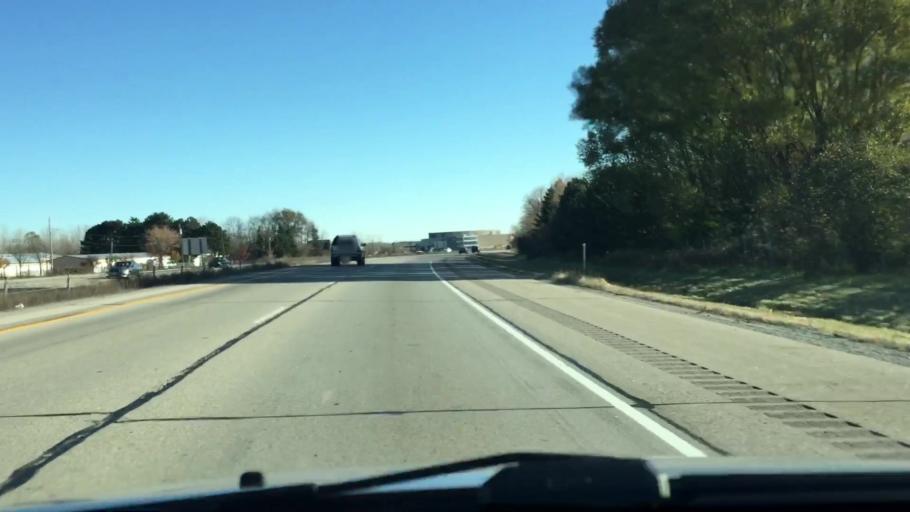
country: US
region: Wisconsin
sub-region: Outagamie County
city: Appleton
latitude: 44.2974
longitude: -88.4594
